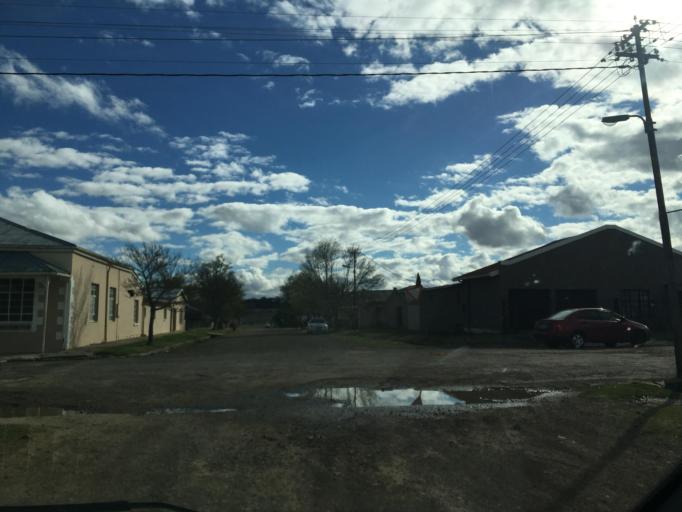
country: ZA
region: Eastern Cape
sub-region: Chris Hani District Municipality
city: Elliot
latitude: -31.3321
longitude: 27.8488
